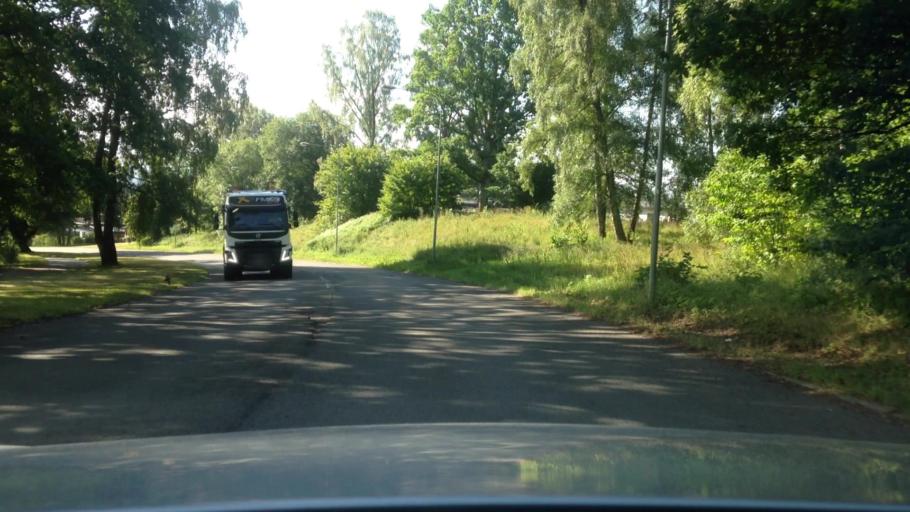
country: SE
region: Vaestra Goetaland
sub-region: Skovde Kommun
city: Skoevde
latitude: 58.3965
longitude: 13.8188
